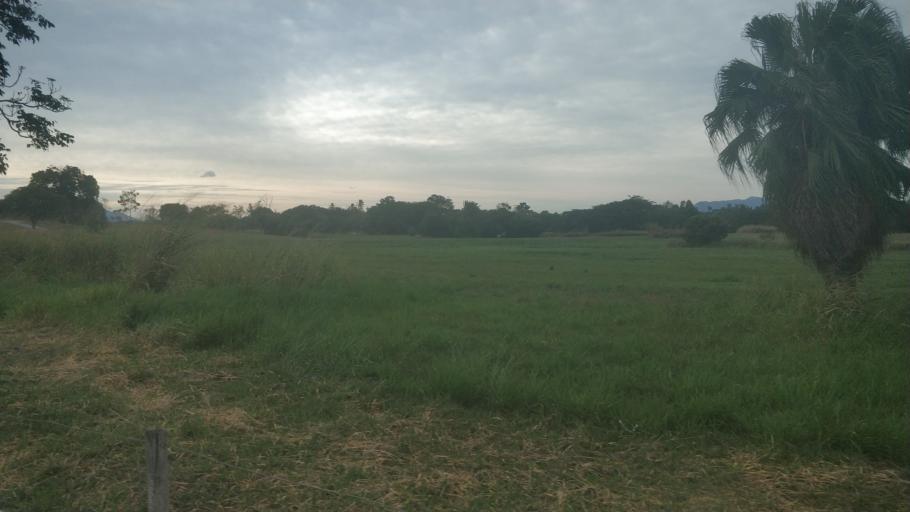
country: BR
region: Rio de Janeiro
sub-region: Seropedica
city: Seropedica
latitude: -22.7610
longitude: -43.6862
